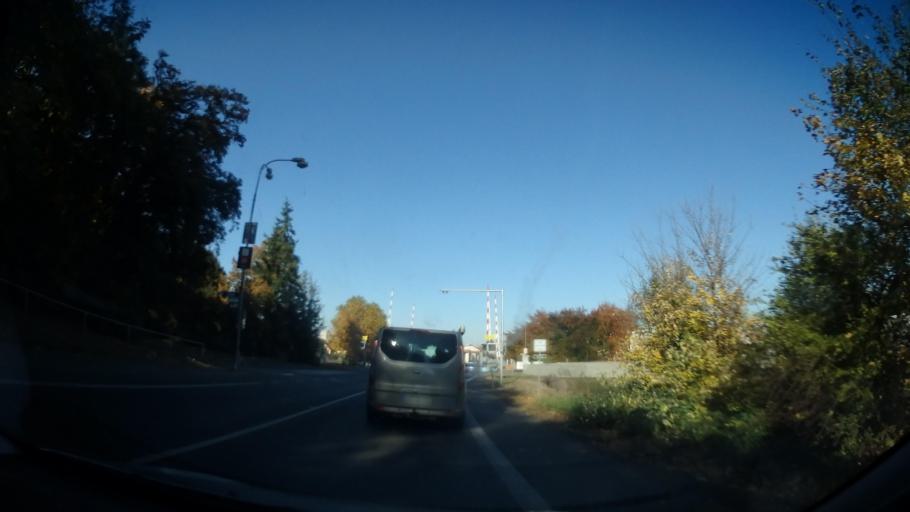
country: CZ
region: Pardubicky
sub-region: Okres Chrudim
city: Chrudim
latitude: 49.9396
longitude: 15.7945
